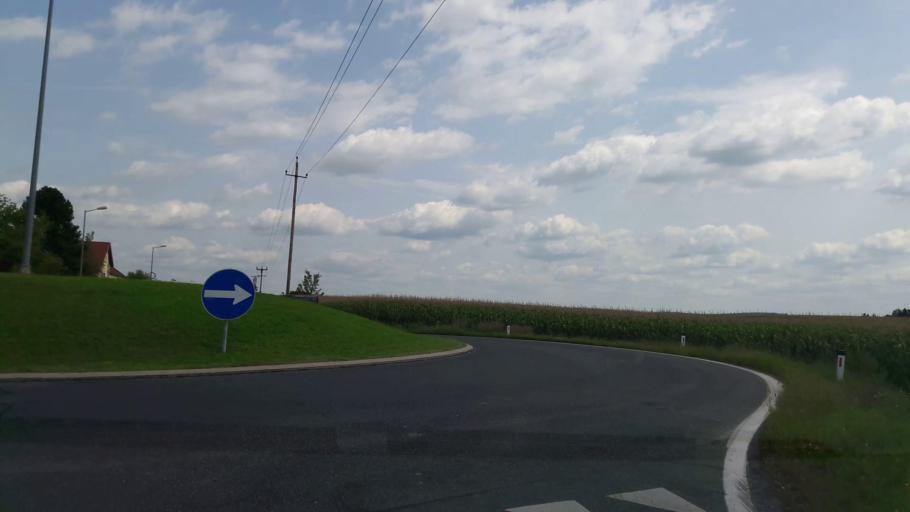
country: AT
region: Styria
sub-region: Politischer Bezirk Hartberg-Fuerstenfeld
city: Hartberg
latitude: 47.2670
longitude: 15.9441
